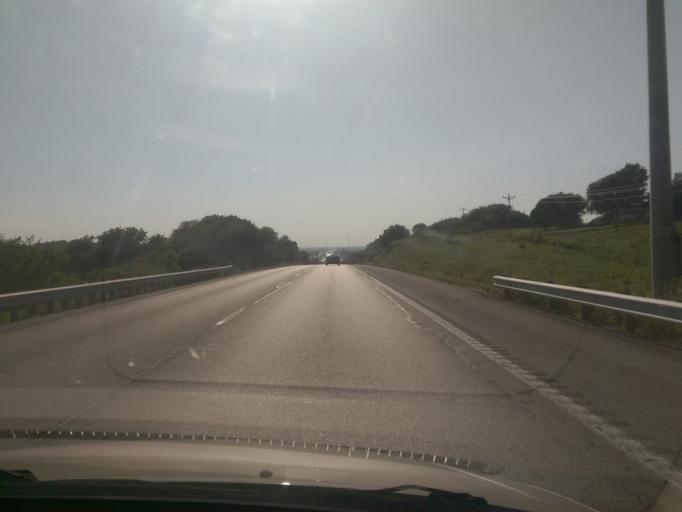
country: US
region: Missouri
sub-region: Lafayette County
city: Odessa
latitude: 39.0082
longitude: -93.9507
